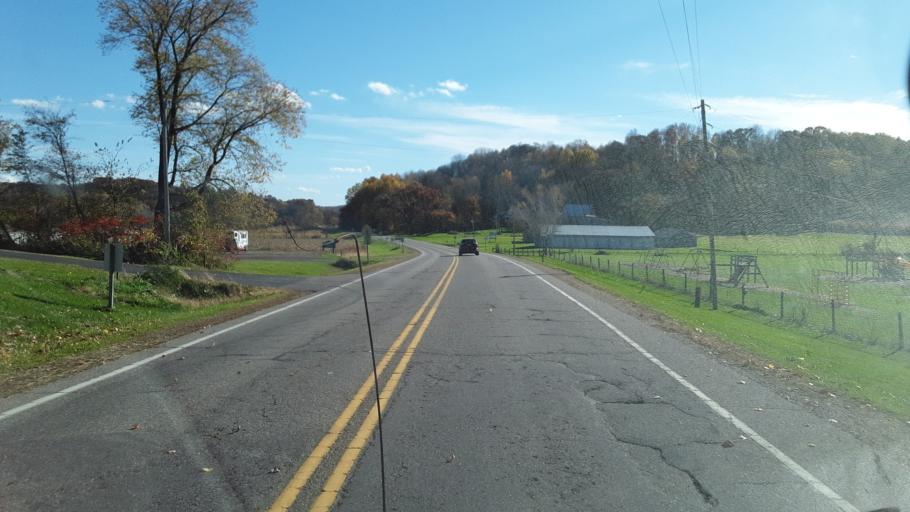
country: US
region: Wisconsin
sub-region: Sauk County
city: Reedsburg
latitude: 43.5784
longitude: -90.1344
